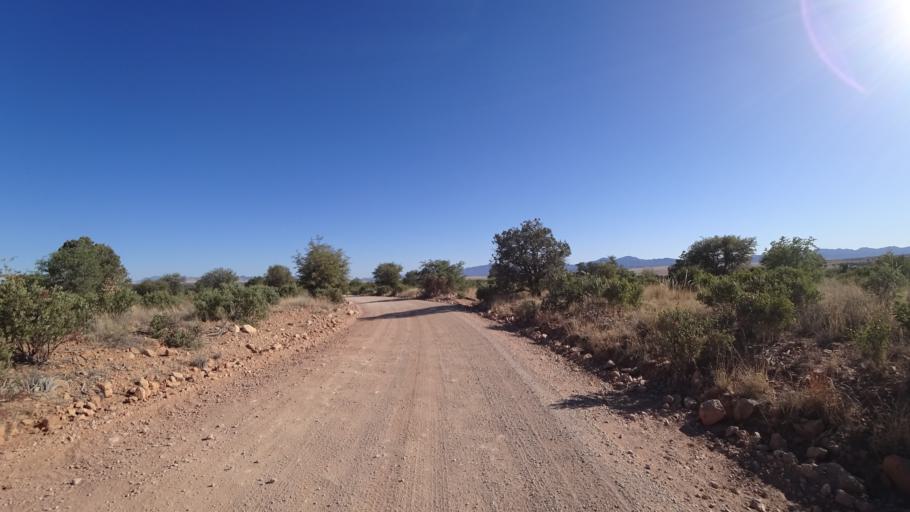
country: MX
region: Sonora
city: Santa Cruz
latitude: 31.4892
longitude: -110.5585
